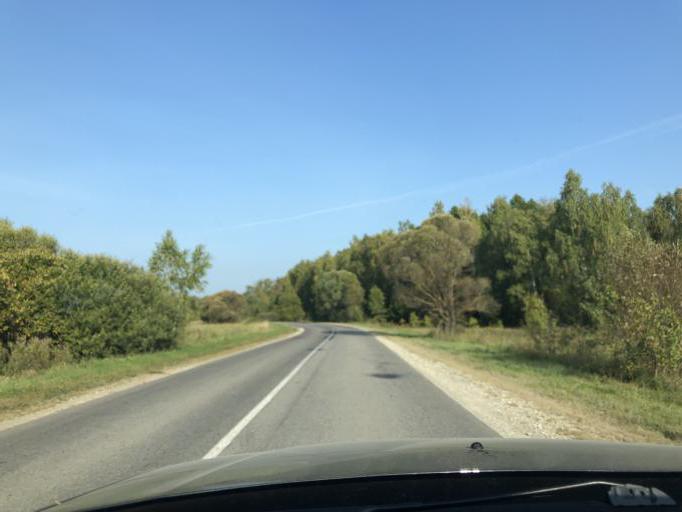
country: RU
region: Tula
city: Leninskiy
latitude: 54.3359
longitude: 37.3812
